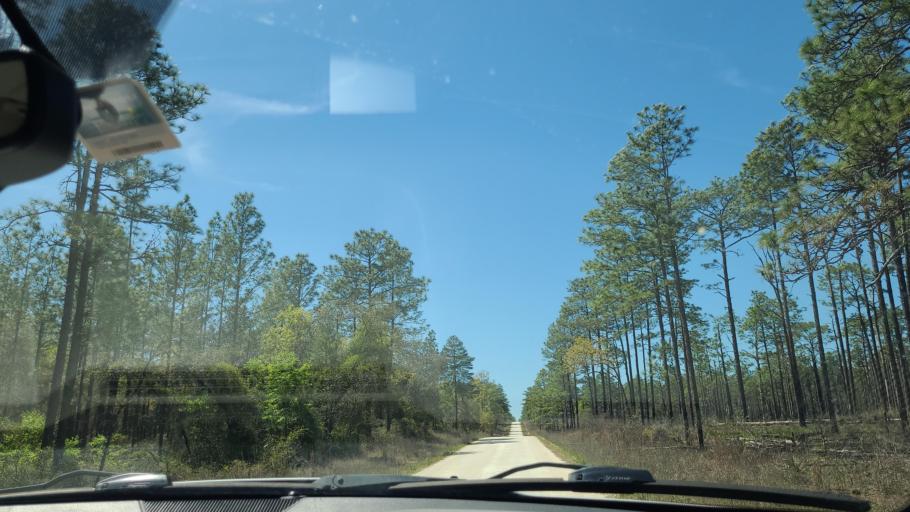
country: US
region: Florida
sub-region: Putnam County
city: Interlachen
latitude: 29.4289
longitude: -81.7978
